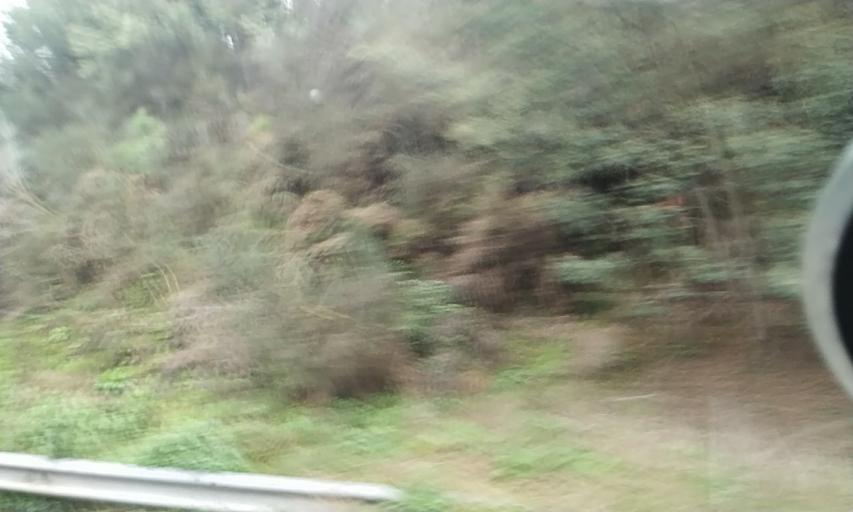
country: PT
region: Porto
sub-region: Amarante
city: Amarante
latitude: 41.3073
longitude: -8.0750
